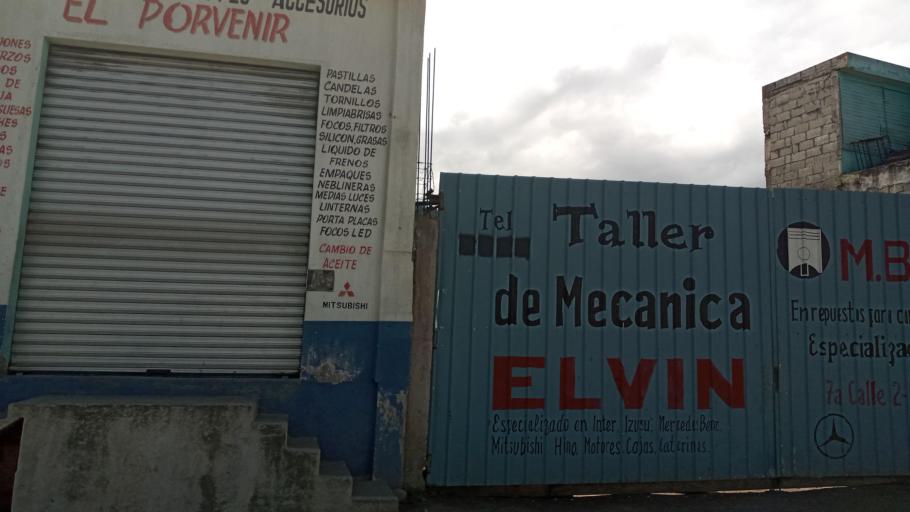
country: GT
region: Quetzaltenango
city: Quetzaltenango
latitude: 14.8421
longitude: -91.5099
